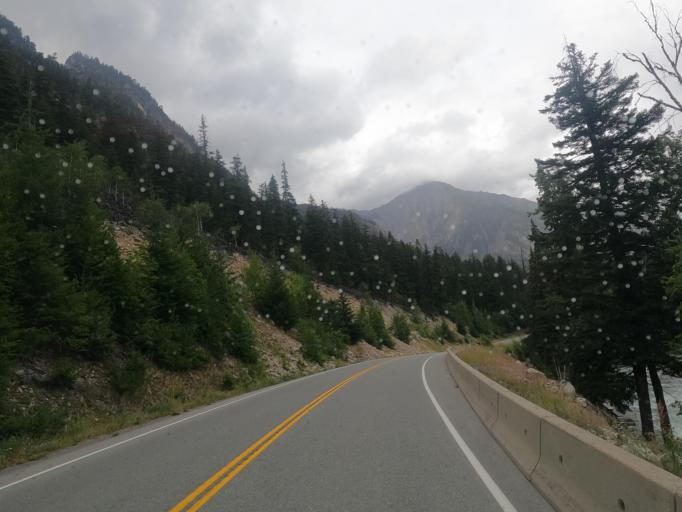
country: CA
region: British Columbia
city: Lillooet
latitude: 50.5152
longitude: -122.1709
